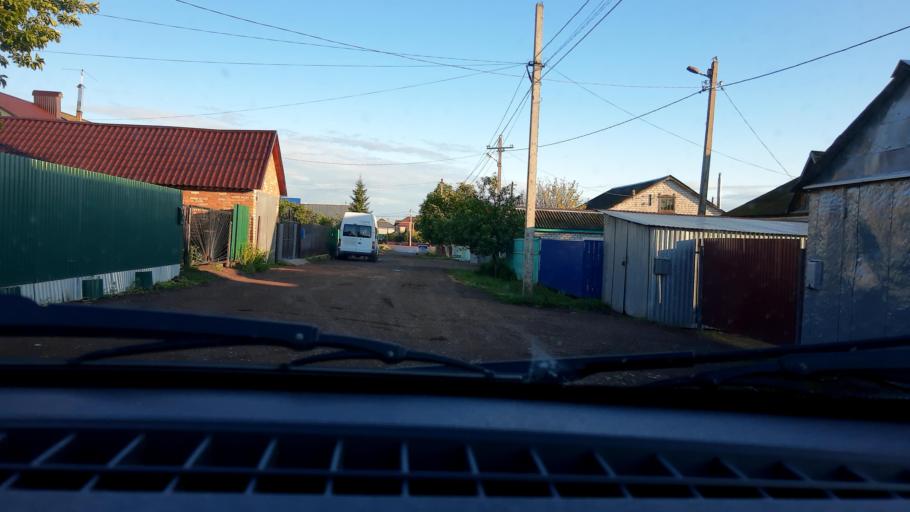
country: RU
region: Bashkortostan
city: Avdon
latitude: 54.8165
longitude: 55.7035
